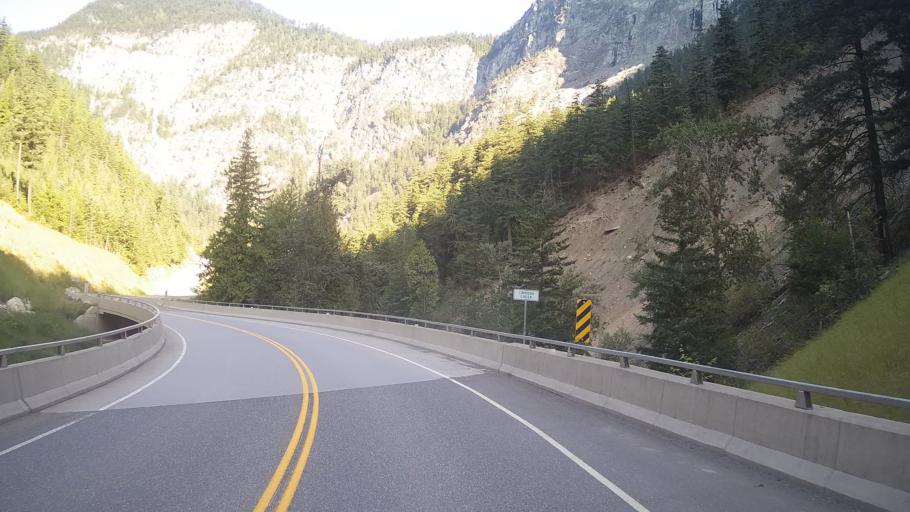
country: CA
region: British Columbia
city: Lillooet
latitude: 50.6428
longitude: -122.0533
